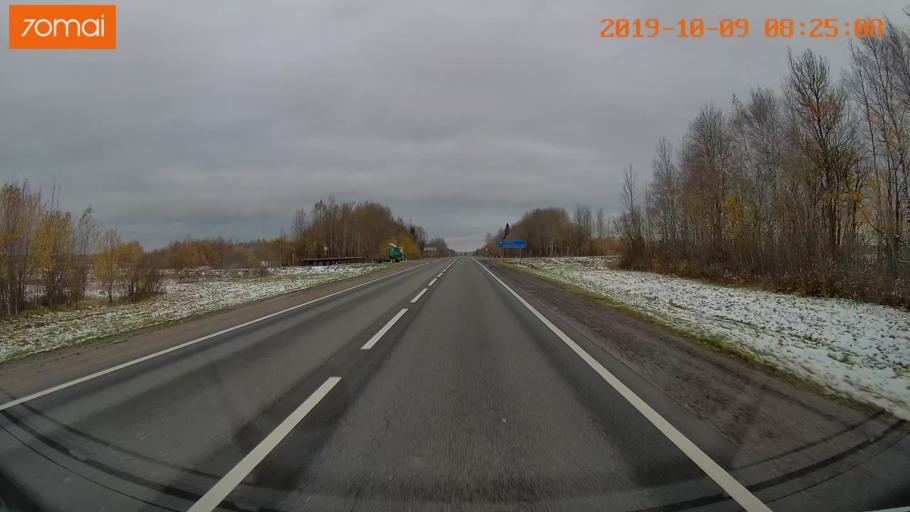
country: RU
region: Vologda
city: Gryazovets
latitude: 58.7766
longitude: 40.2741
